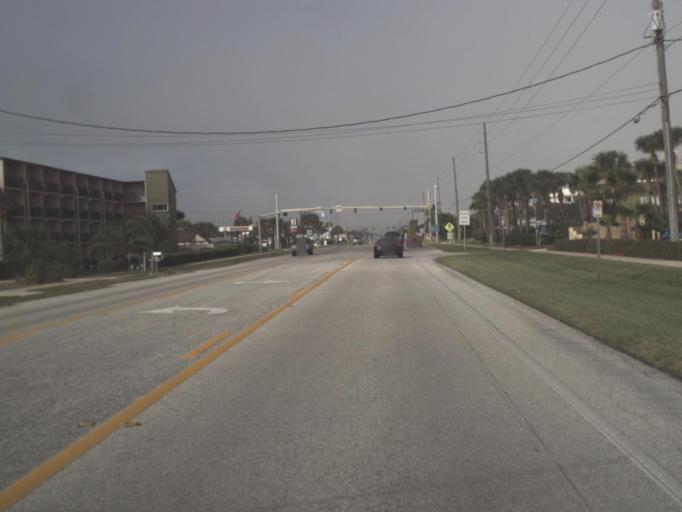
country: US
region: Florida
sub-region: Volusia County
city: Edgewater
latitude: 29.0077
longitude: -80.8784
